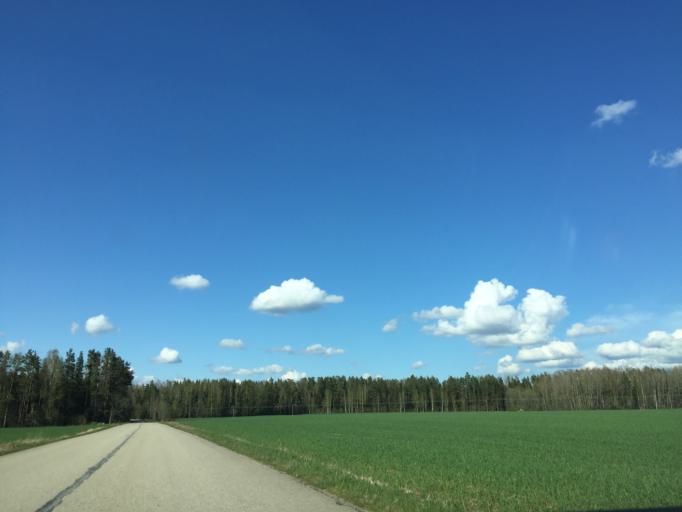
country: LV
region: Beverina
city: Murmuiza
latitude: 57.4941
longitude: 25.5693
